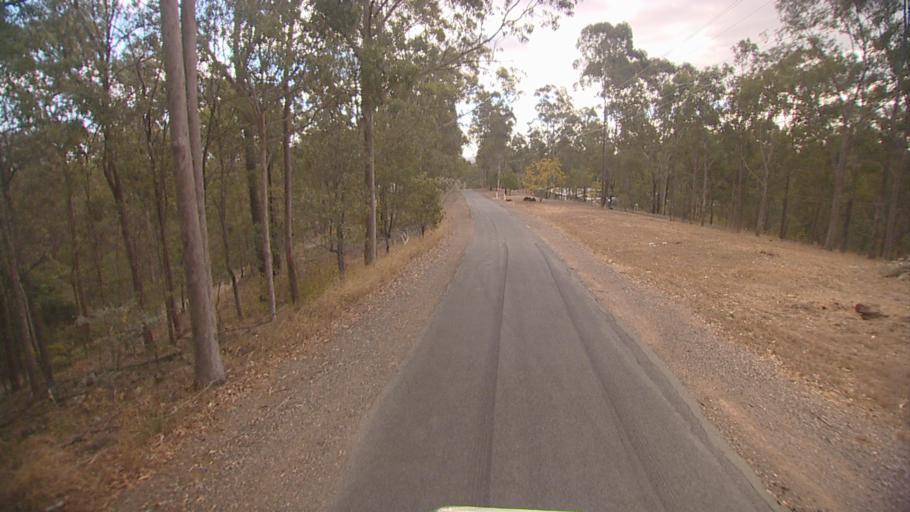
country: AU
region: Queensland
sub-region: Logan
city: Cedar Vale
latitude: -27.8938
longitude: 153.0333
